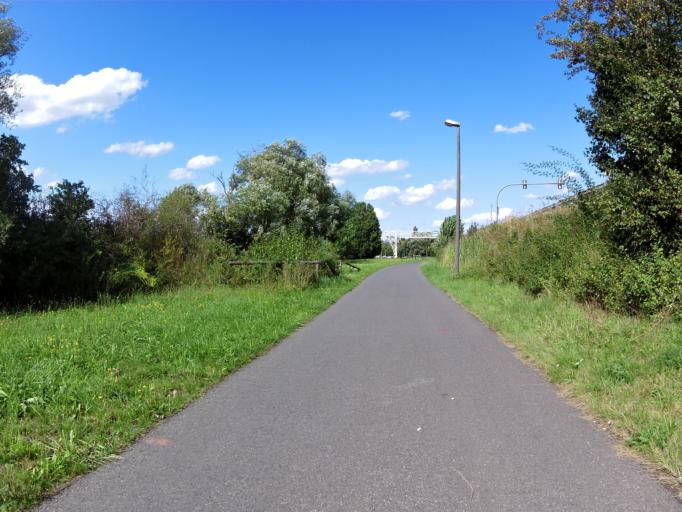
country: DE
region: Bavaria
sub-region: Regierungsbezirk Unterfranken
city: Kitzingen
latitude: 49.7260
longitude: 10.1651
